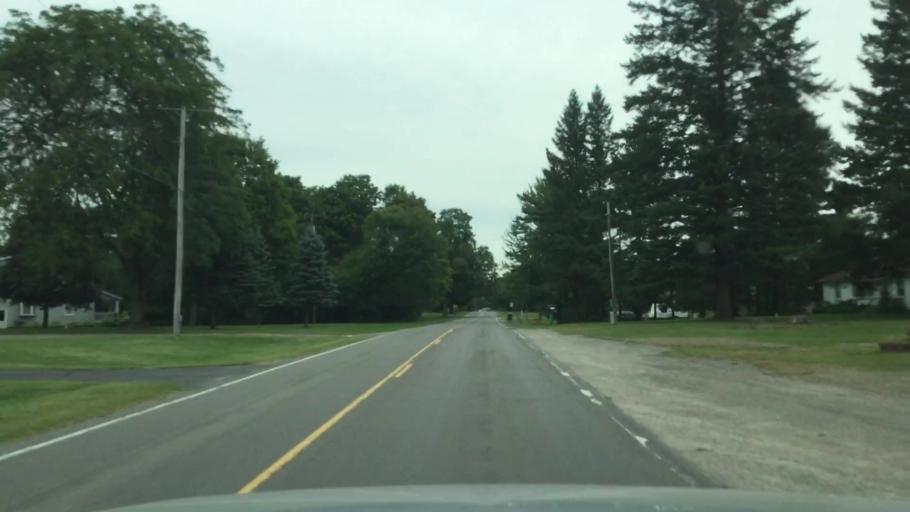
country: US
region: Michigan
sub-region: Washtenaw County
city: Milan
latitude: 42.1601
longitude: -83.6513
